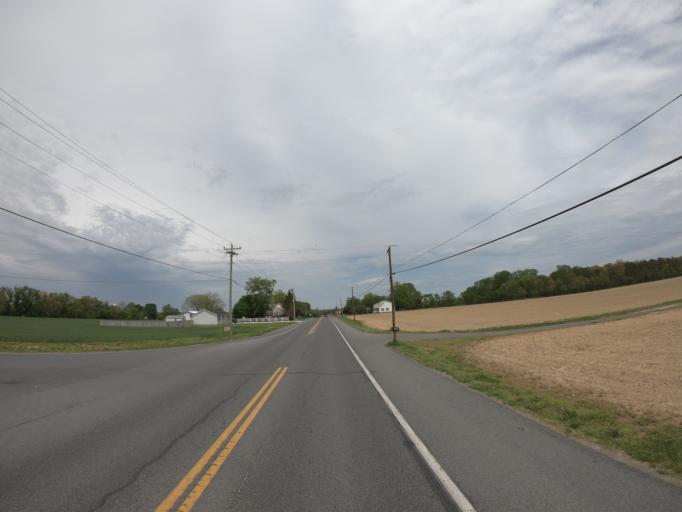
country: US
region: Delaware
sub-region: Sussex County
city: Milton
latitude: 38.8019
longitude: -75.2769
